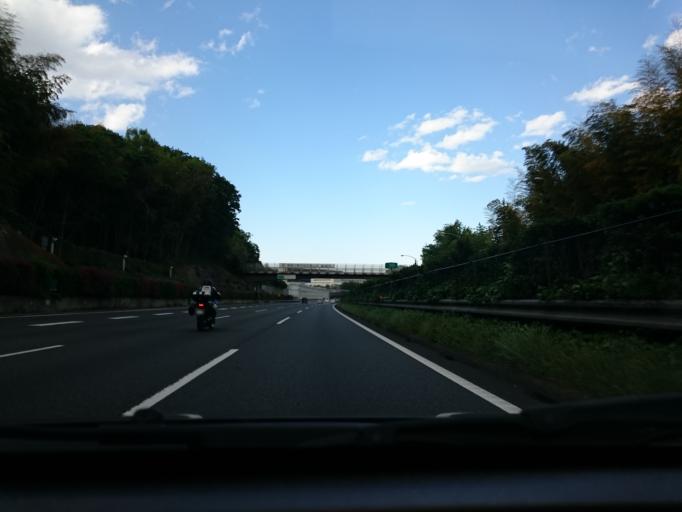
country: JP
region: Kanagawa
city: Atsugi
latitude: 35.4412
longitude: 139.4081
